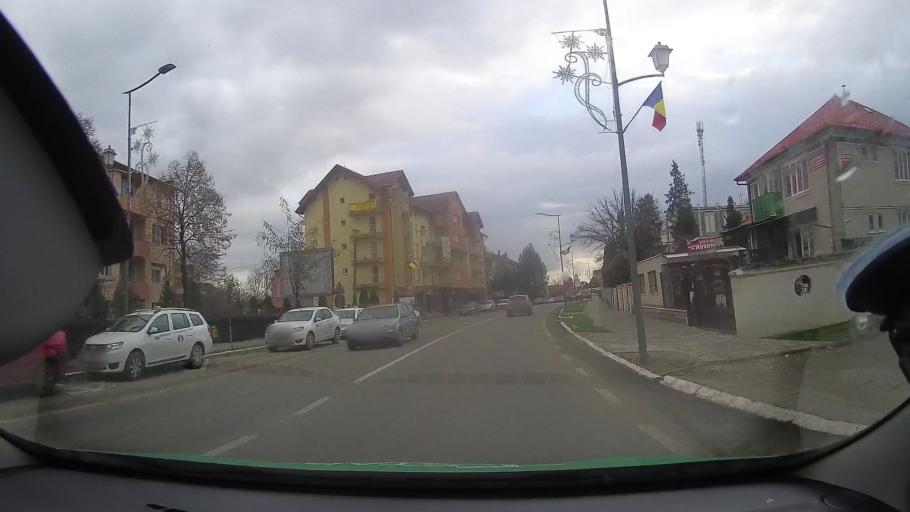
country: RO
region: Cluj
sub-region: Municipiul Campia Turzii
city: Campia Turzii
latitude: 46.5418
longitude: 23.8893
